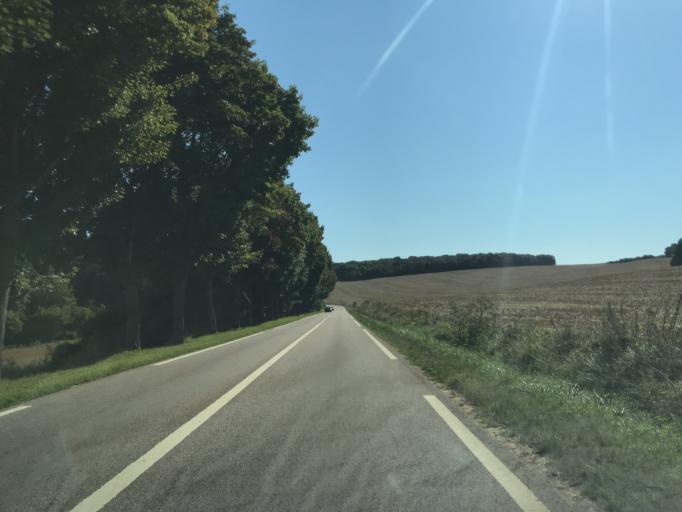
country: FR
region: Ile-de-France
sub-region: Departement du Val-d'Oise
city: Magny-en-Vexin
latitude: 49.1432
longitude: 1.7485
